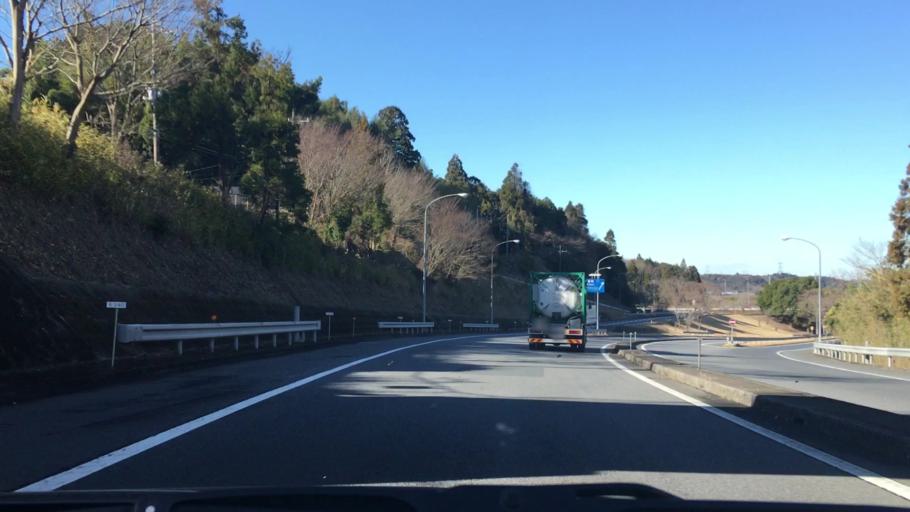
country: JP
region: Chiba
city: Sawara
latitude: 35.8412
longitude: 140.4456
